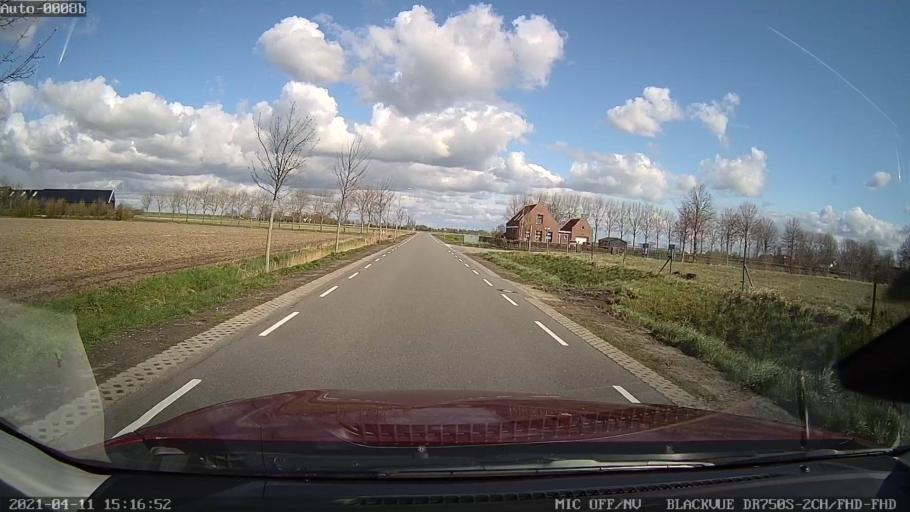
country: NL
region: Zeeland
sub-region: Schouwen-Duiveland
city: Bruinisse
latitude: 51.6791
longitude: 4.0322
